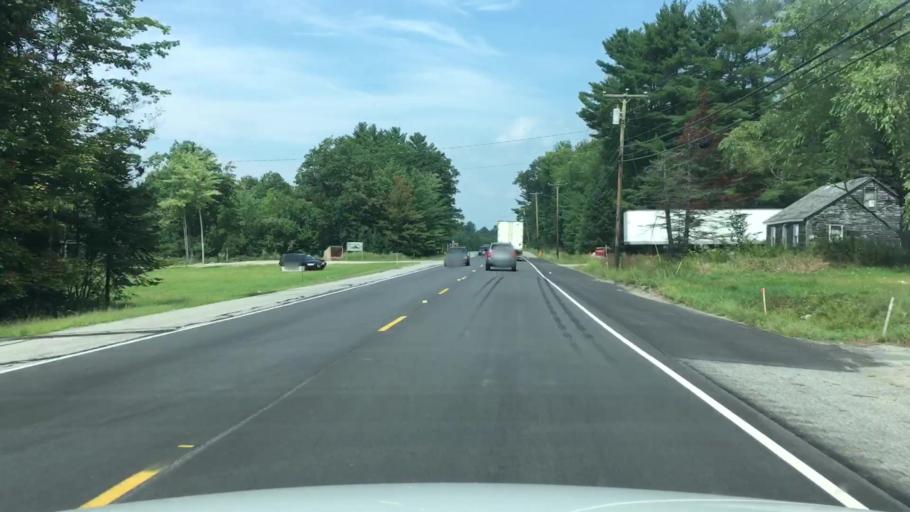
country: US
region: Maine
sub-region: Androscoggin County
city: Turner
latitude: 44.2216
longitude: -70.2483
